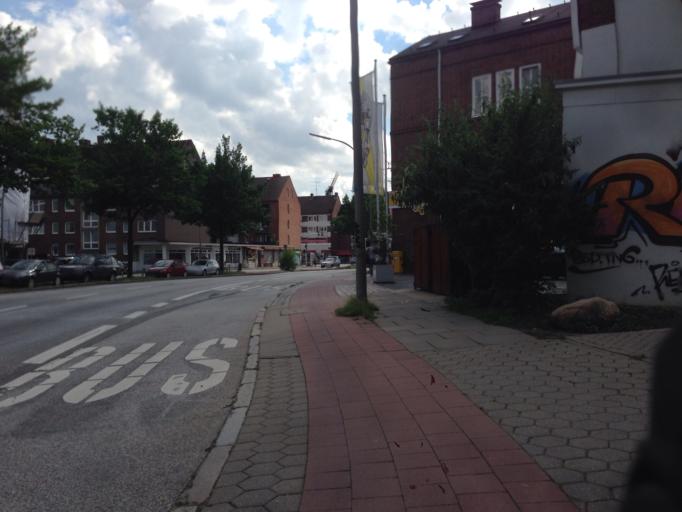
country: DE
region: Hamburg
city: Hamburg-Nord
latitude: 53.5848
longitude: 9.9711
